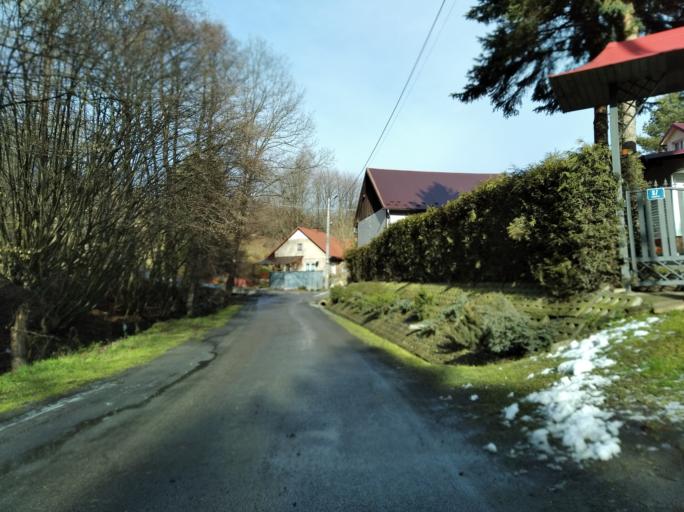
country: PL
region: Subcarpathian Voivodeship
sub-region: Powiat strzyzowski
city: Strzyzow
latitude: 49.9008
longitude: 21.7522
